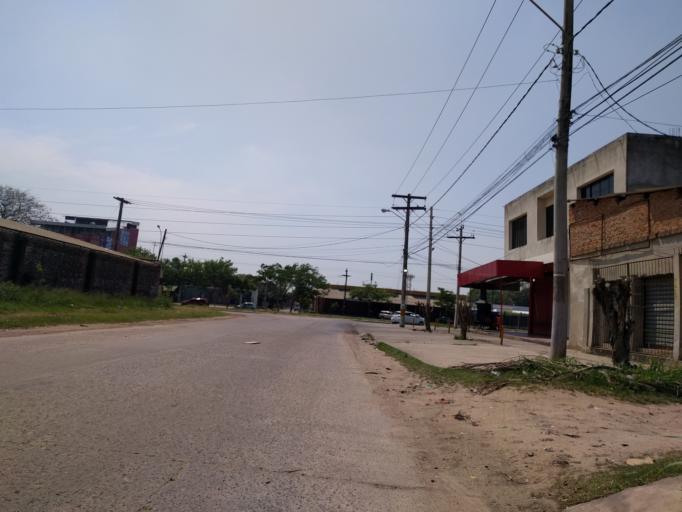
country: BO
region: Santa Cruz
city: Santa Cruz de la Sierra
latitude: -17.7910
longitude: -63.1493
